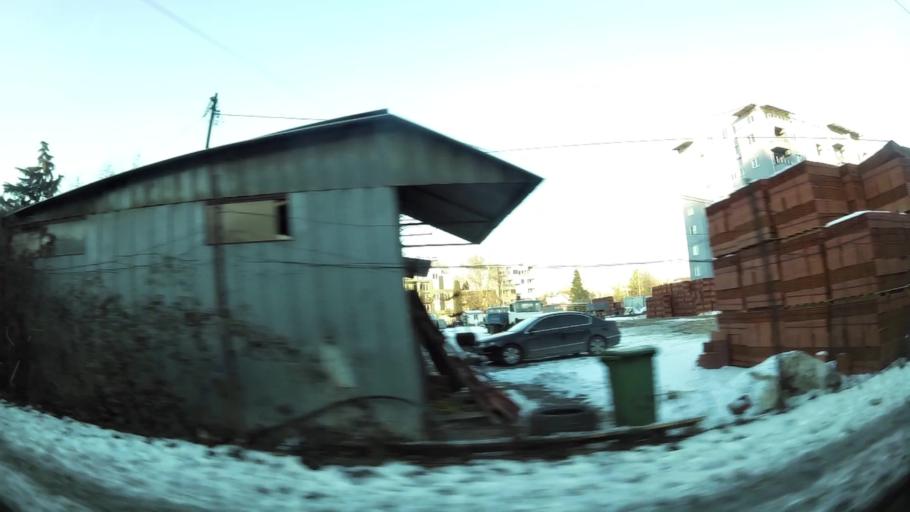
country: MK
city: Krushopek
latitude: 41.9984
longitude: 21.3834
